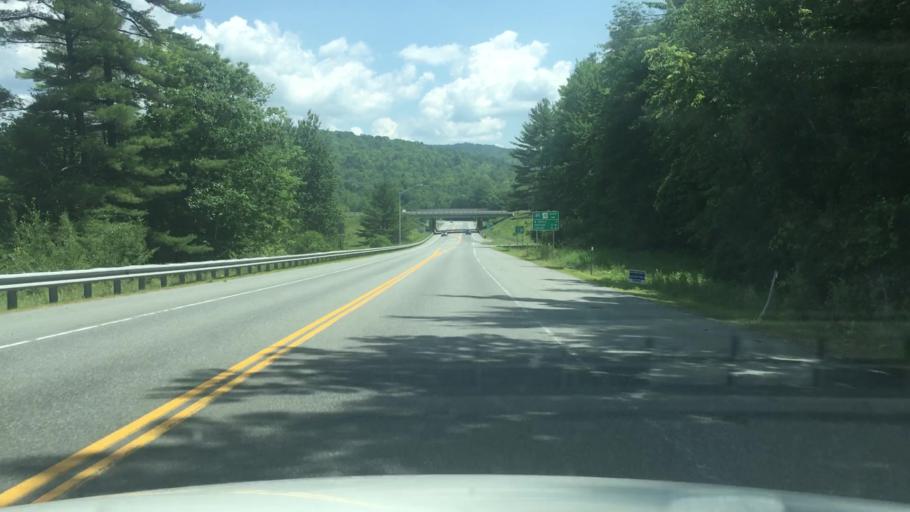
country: US
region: New Hampshire
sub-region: Grafton County
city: Lebanon
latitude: 43.6366
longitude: -72.2157
